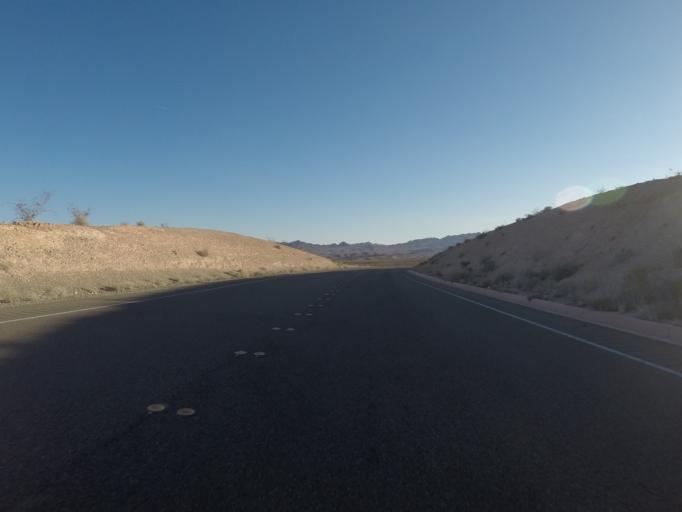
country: US
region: Nevada
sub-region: Clark County
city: Moapa Valley
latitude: 36.3271
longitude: -114.4923
